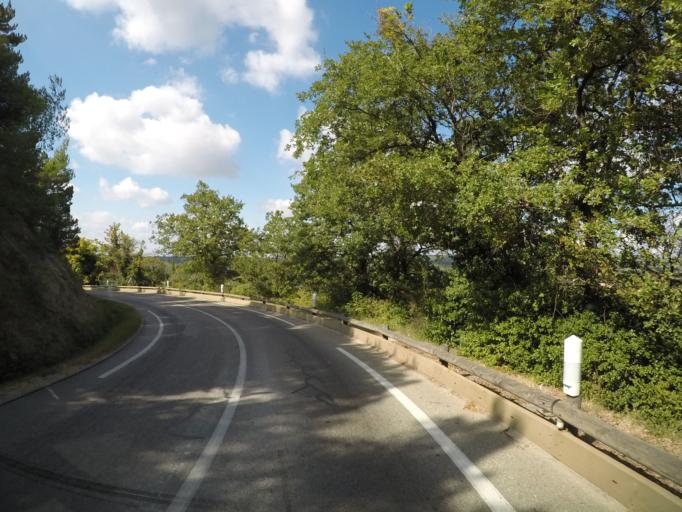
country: FR
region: Provence-Alpes-Cote d'Azur
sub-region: Departement du Vaucluse
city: Visan
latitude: 44.2807
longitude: 4.9945
